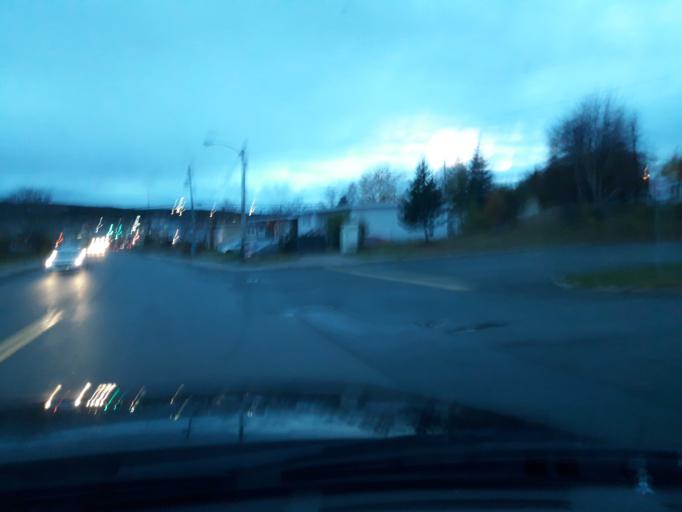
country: CA
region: Newfoundland and Labrador
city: St. John's
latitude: 47.5643
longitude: -52.7546
